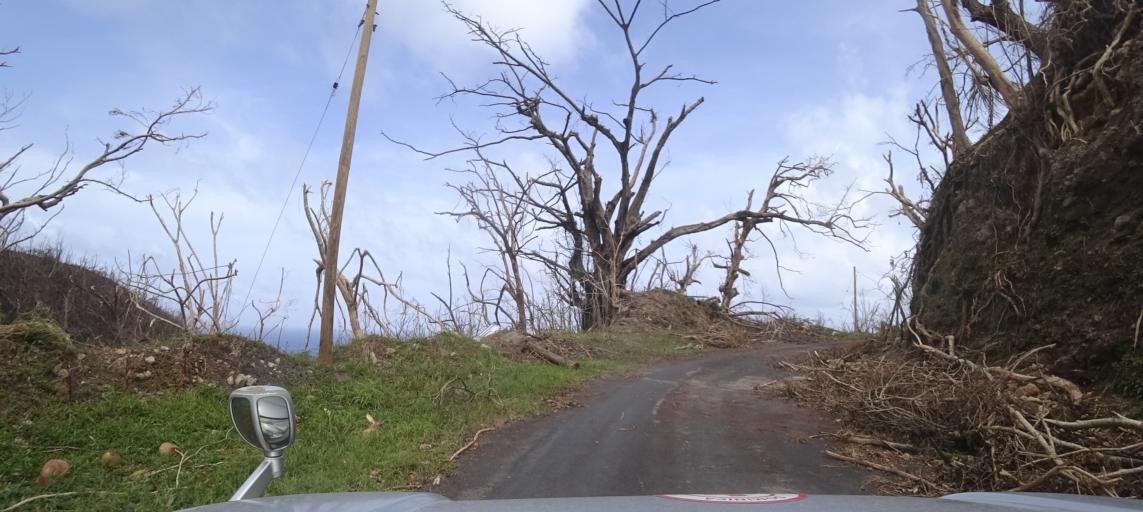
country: DM
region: Saint Patrick
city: La Plaine
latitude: 15.3111
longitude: -61.2481
